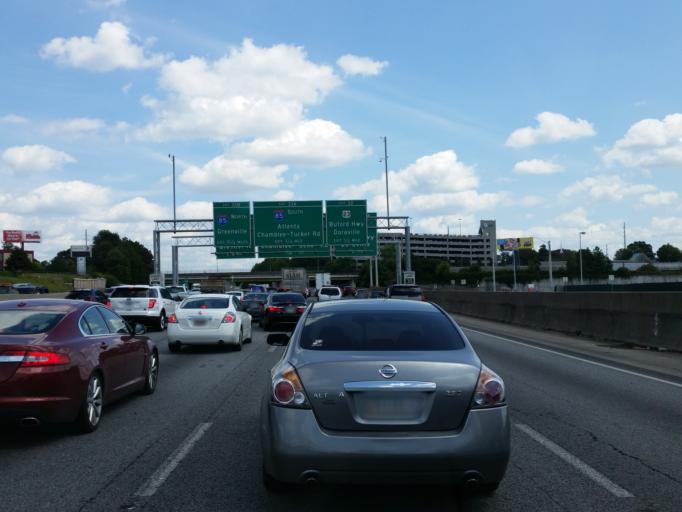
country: US
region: Georgia
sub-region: DeKalb County
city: Doraville
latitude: 33.9071
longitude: -84.2805
